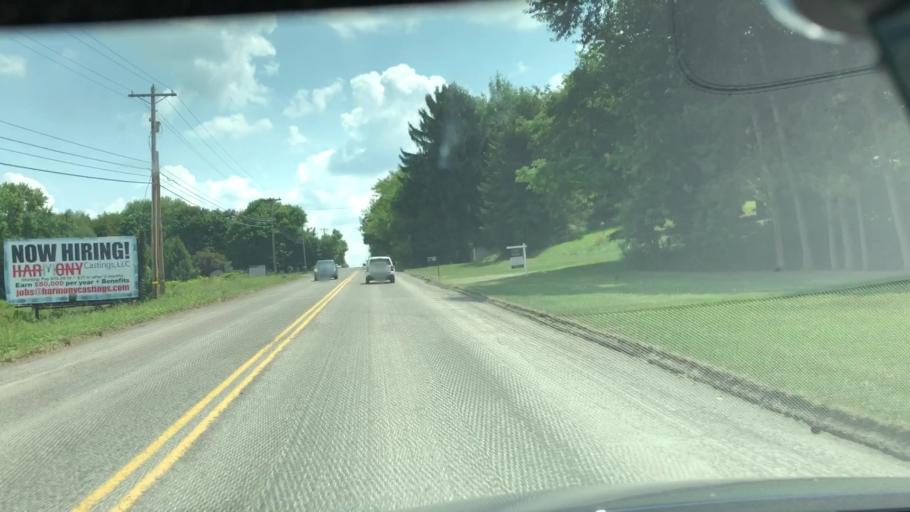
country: US
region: Pennsylvania
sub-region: Butler County
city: Saxonburg
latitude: 40.8014
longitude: -79.8250
